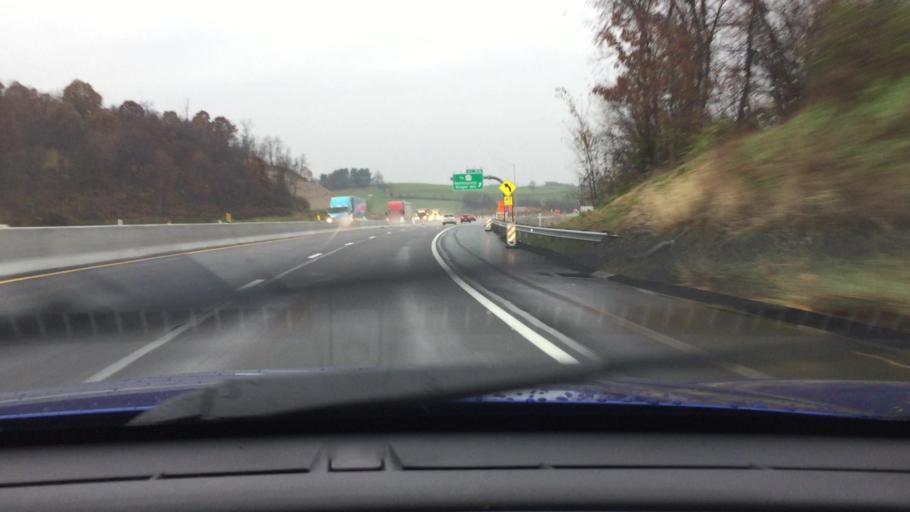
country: US
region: Pennsylvania
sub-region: Washington County
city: Bentleyville
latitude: 40.1299
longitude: -79.9900
